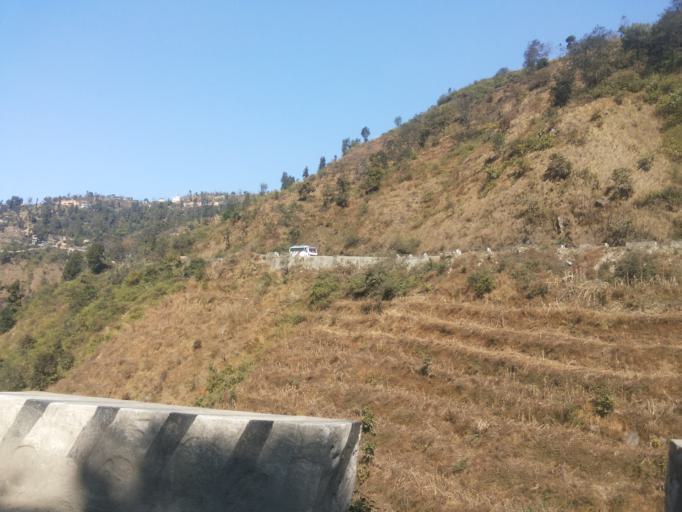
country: NP
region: Central Region
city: Kirtipur
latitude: 27.7073
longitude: 85.2001
